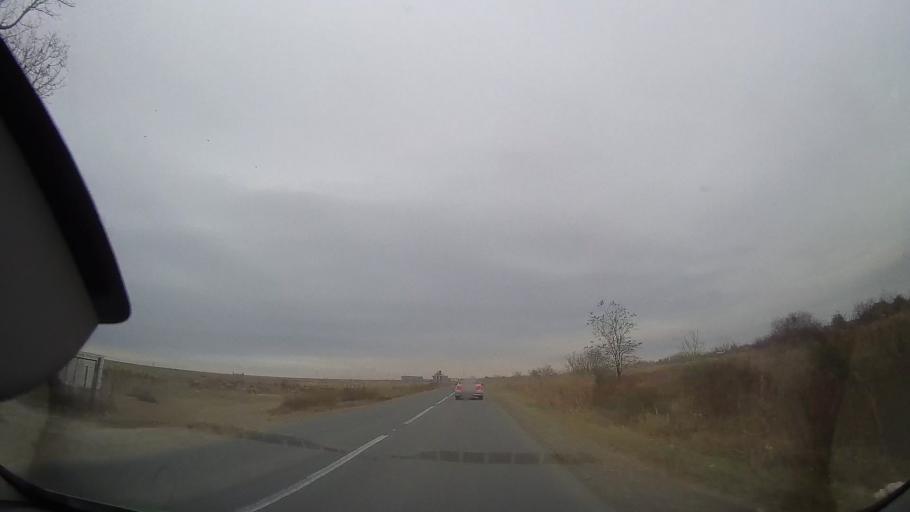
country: RO
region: Ialomita
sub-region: Oras Amara
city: Amara
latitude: 44.6223
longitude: 27.3014
